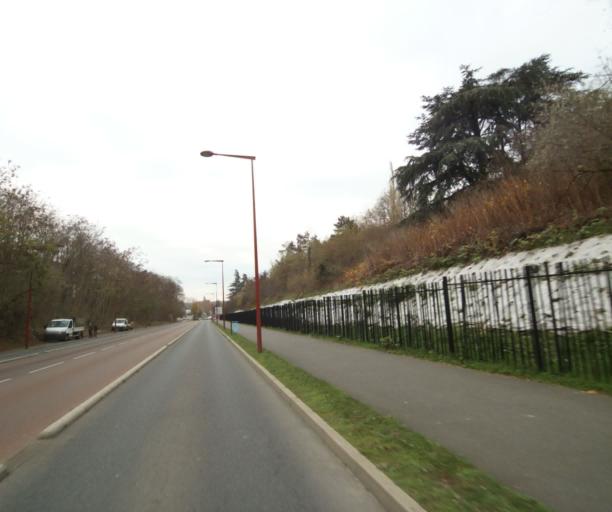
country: FR
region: Ile-de-France
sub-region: Departement du Val-d'Oise
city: Gonesse
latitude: 48.9846
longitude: 2.4638
